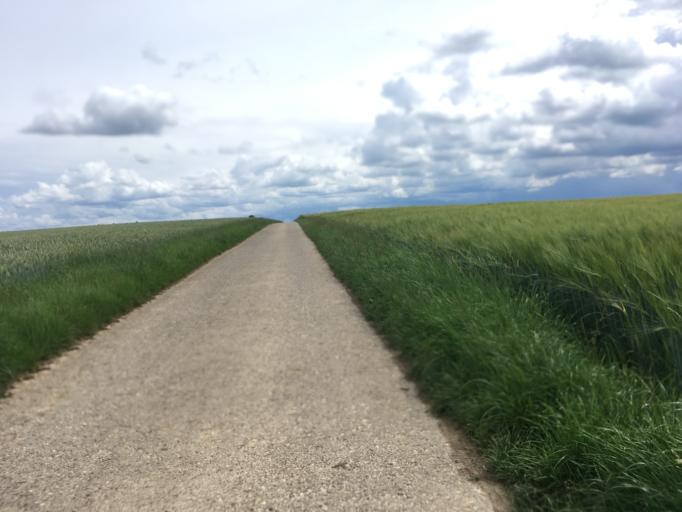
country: DE
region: Baden-Wuerttemberg
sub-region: Regierungsbezirk Stuttgart
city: Bietigheim-Bissingen
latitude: 48.9545
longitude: 9.0937
